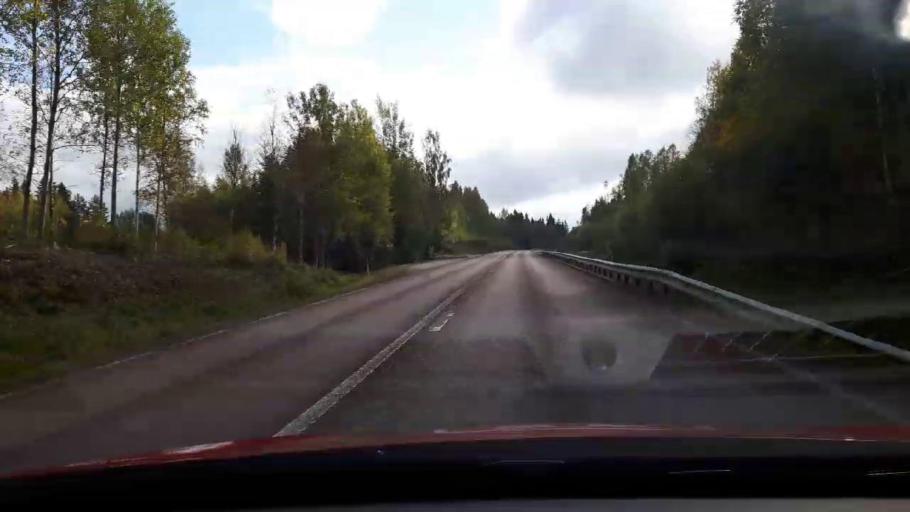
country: SE
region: Gaevleborg
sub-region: Ljusdals Kommun
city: Jaervsoe
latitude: 61.6212
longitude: 16.2880
